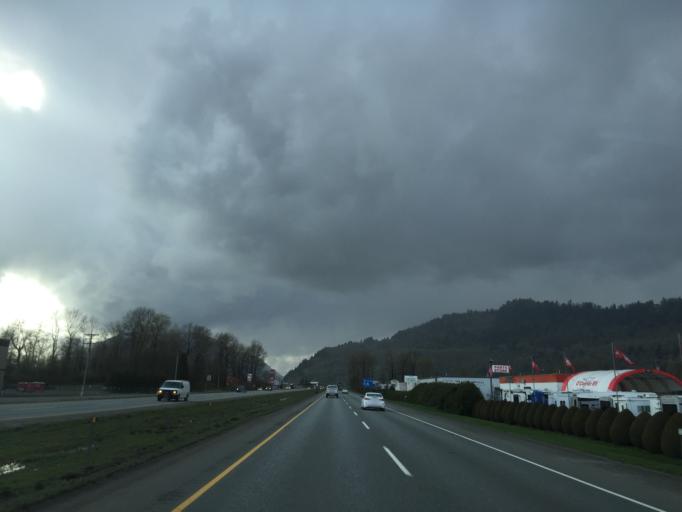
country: CA
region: British Columbia
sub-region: Fraser Valley Regional District
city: Chilliwack
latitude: 49.1442
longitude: -121.9936
